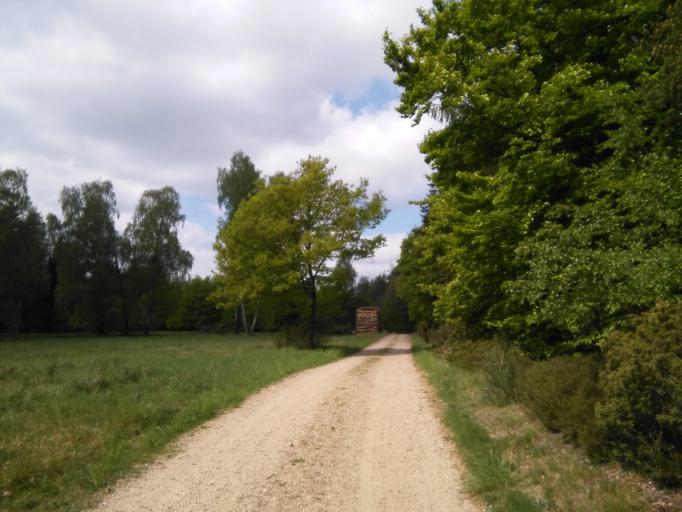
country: DK
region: Central Jutland
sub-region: Silkeborg Kommune
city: Svejbaek
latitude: 56.0620
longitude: 9.6319
